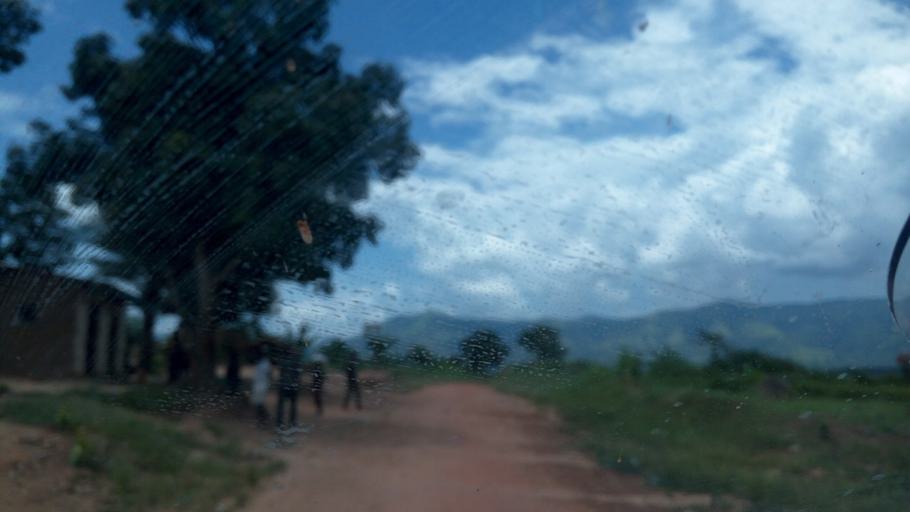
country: TZ
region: Kigoma
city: Kigoma
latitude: -4.9464
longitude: 28.7434
